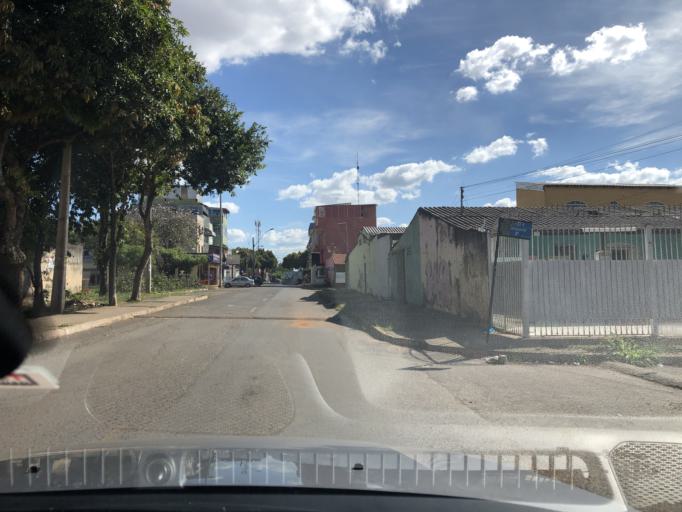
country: BR
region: Federal District
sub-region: Brasilia
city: Brasilia
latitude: -15.7956
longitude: -48.1194
